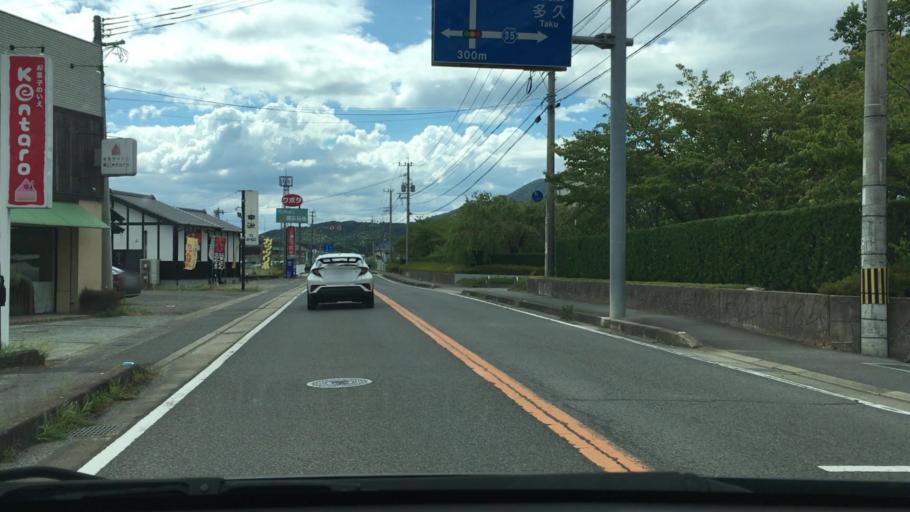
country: JP
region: Saga Prefecture
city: Kashima
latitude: 33.2202
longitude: 130.1558
